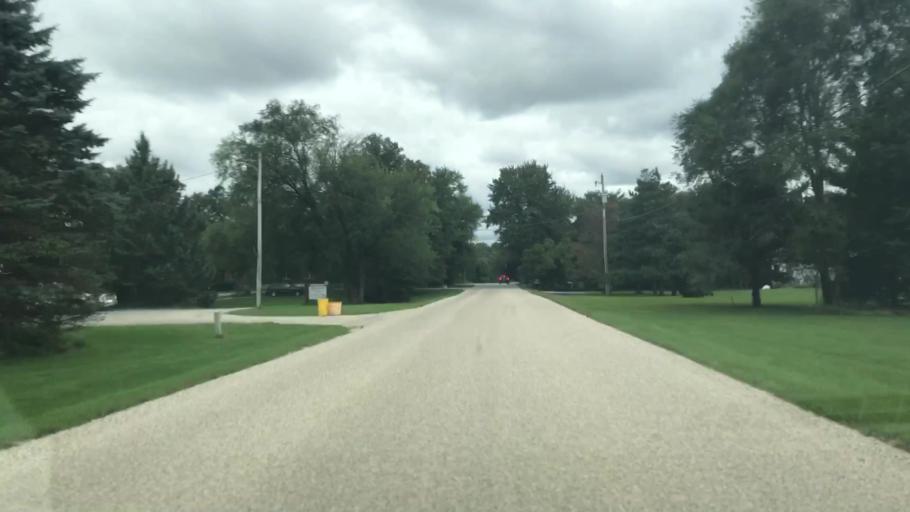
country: US
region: Wisconsin
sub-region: Waukesha County
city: North Prairie
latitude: 42.9166
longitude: -88.4368
